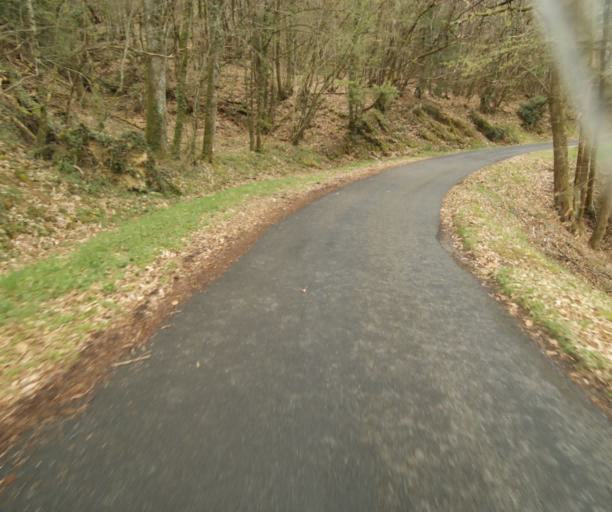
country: FR
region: Limousin
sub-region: Departement de la Correze
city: Naves
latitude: 45.2993
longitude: 1.8110
